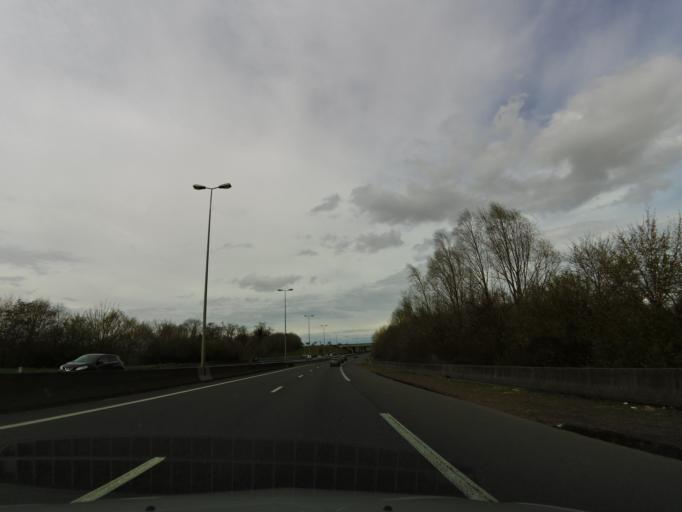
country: FR
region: Lower Normandy
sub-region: Departement du Calvados
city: Bretteville-sur-Odon
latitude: 49.1590
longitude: -0.4263
